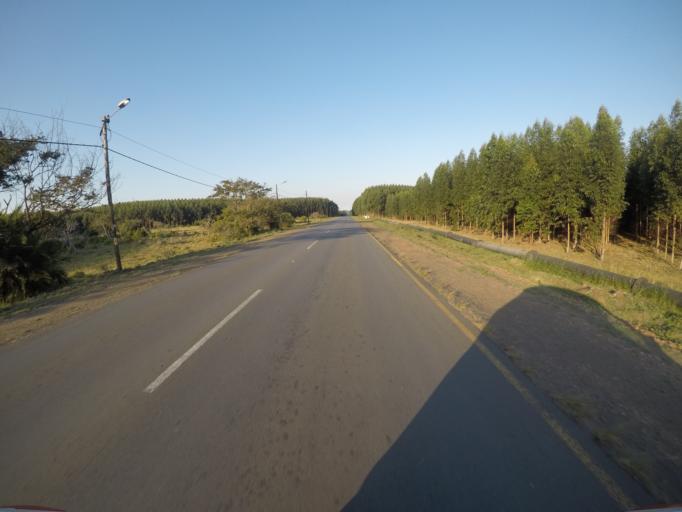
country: ZA
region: KwaZulu-Natal
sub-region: uThungulu District Municipality
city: KwaMbonambi
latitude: -28.6832
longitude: 32.1749
